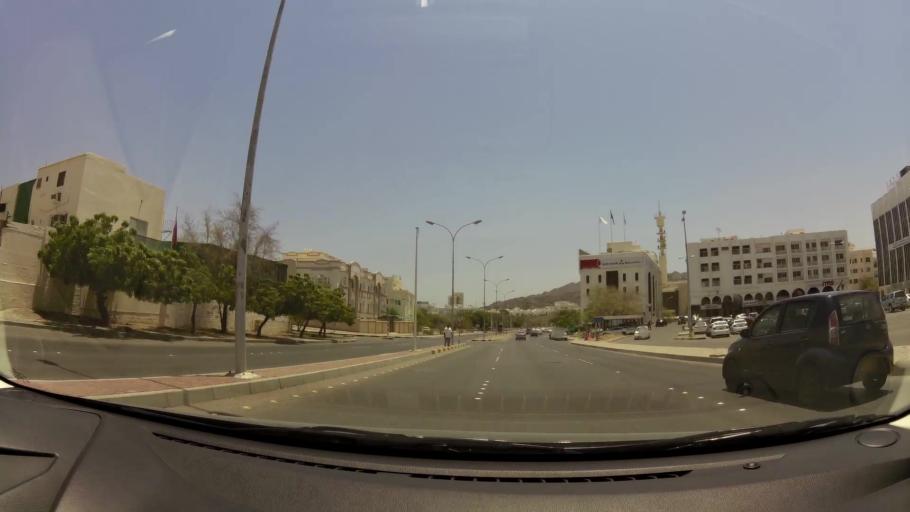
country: OM
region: Muhafazat Masqat
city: Muscat
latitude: 23.6042
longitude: 58.5427
